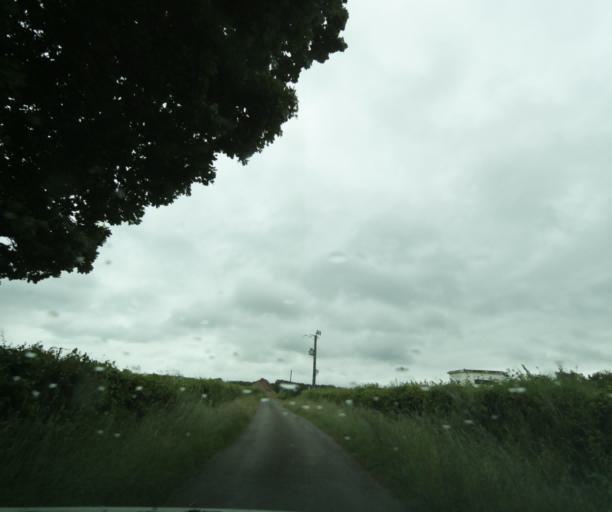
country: FR
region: Bourgogne
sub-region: Departement de Saone-et-Loire
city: Charolles
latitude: 46.4899
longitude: 4.2481
